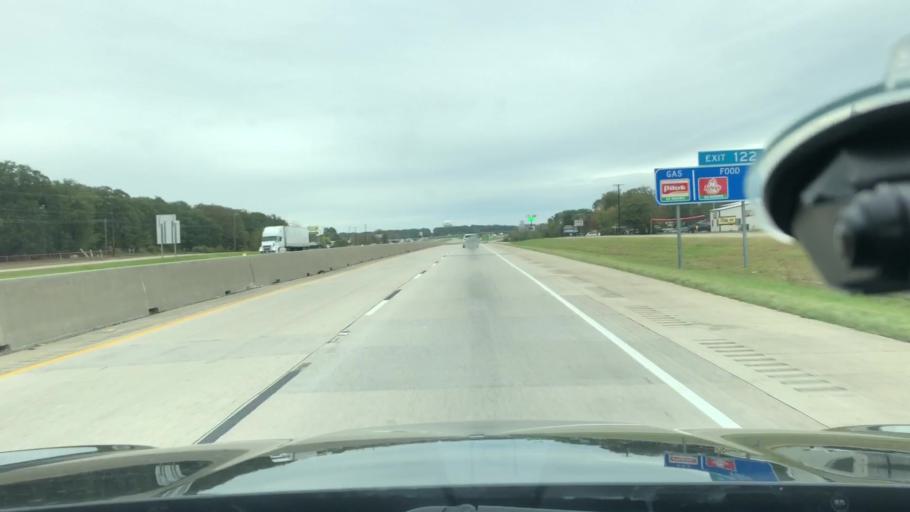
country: US
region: Texas
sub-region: Hopkins County
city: Sulphur Springs
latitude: 33.1206
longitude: -95.6496
